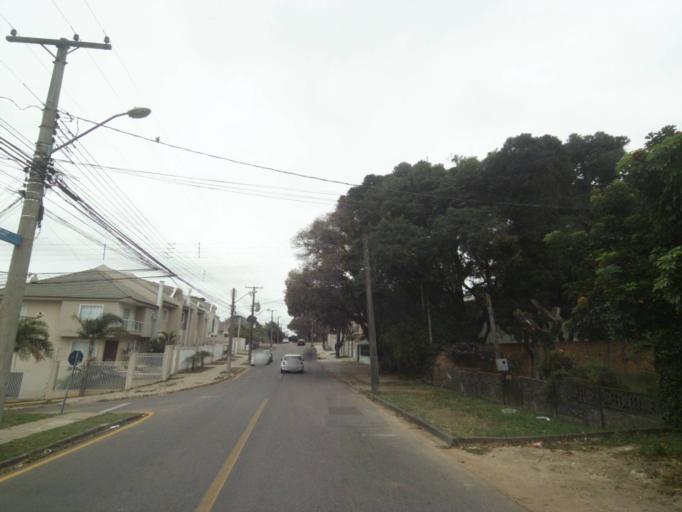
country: BR
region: Parana
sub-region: Pinhais
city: Pinhais
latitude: -25.4783
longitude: -49.2312
